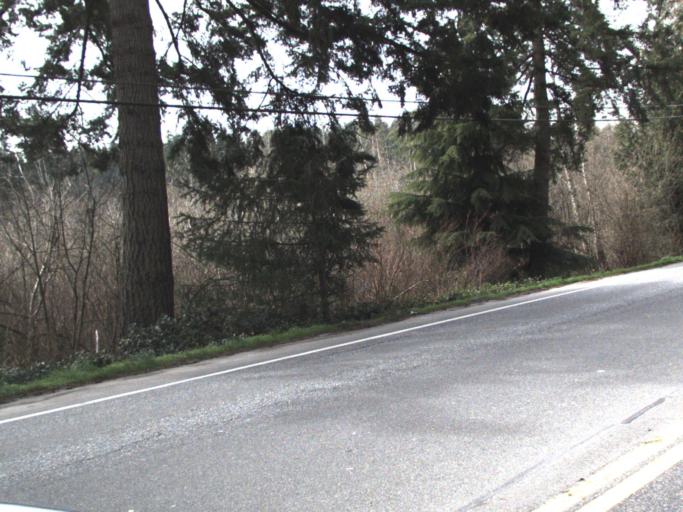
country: US
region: Washington
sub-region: King County
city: Lake Morton-Berrydale
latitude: 47.3581
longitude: -122.0734
